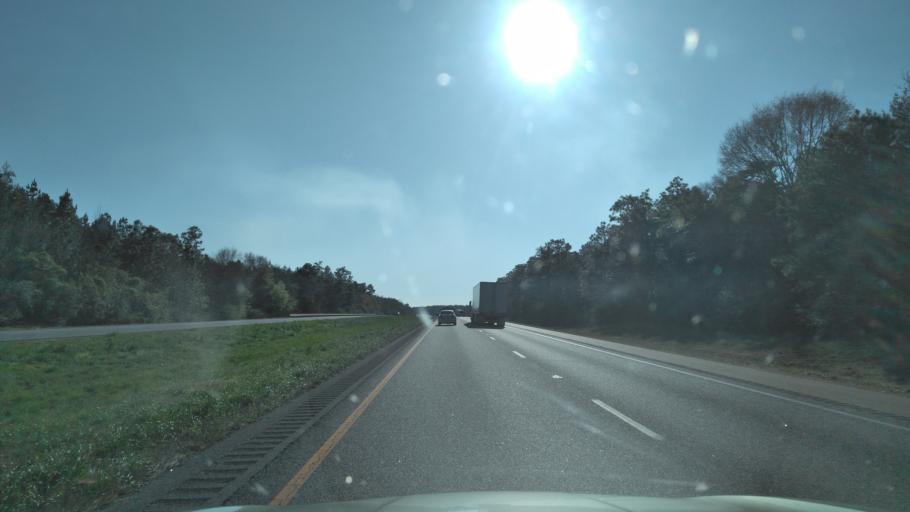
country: US
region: Alabama
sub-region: Escambia County
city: Flomaton
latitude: 31.2322
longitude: -87.2733
